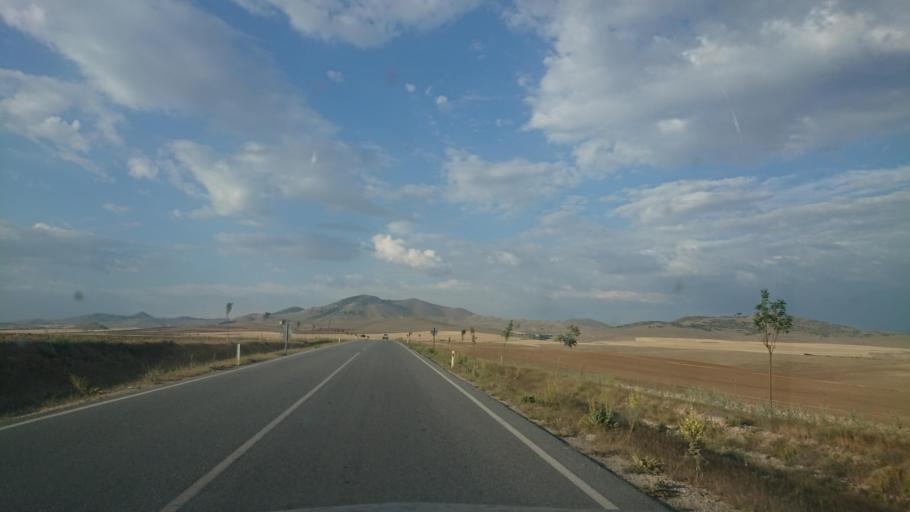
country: TR
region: Aksaray
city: Aksaray
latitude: 38.5064
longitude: 34.0819
